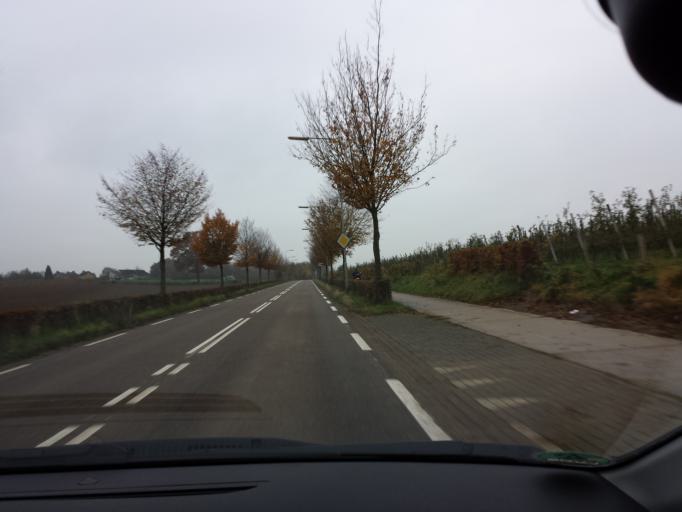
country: NL
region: Limburg
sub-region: Gemeente Simpelveld
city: Simpelveld
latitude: 50.8484
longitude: 5.9765
